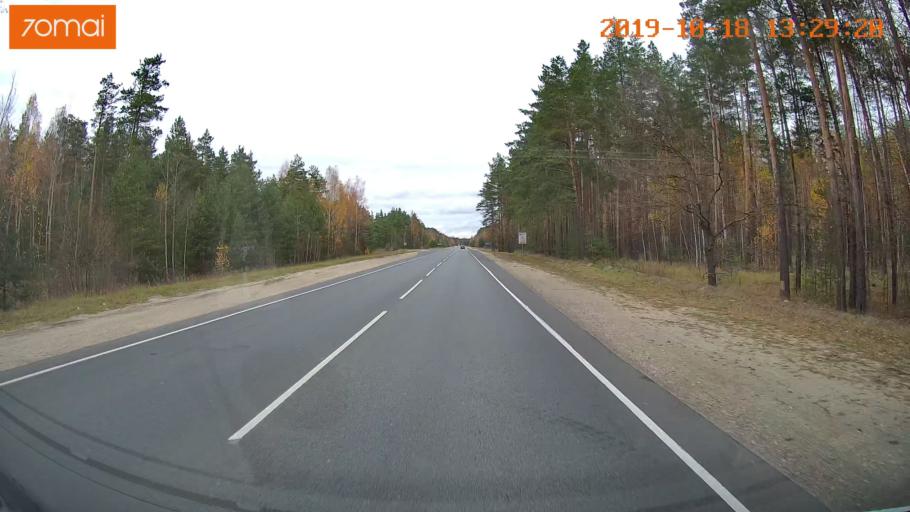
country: RU
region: Rjazan
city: Solotcha
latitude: 54.7930
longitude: 39.8742
